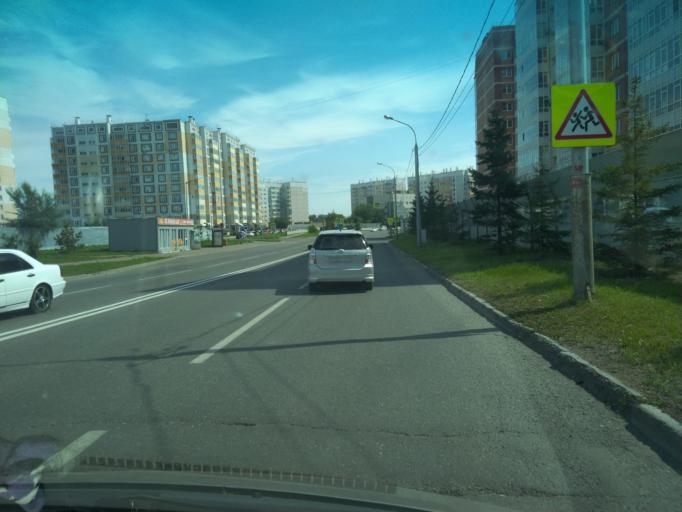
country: RU
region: Krasnoyarskiy
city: Solnechnyy
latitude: 56.0545
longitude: 92.9200
